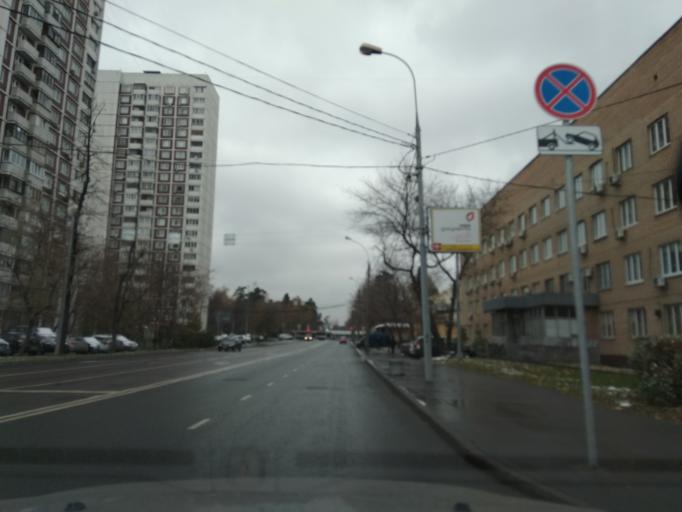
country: RU
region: Moscow
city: Pokrovskoye-Streshnevo
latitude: 55.8088
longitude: 37.4763
